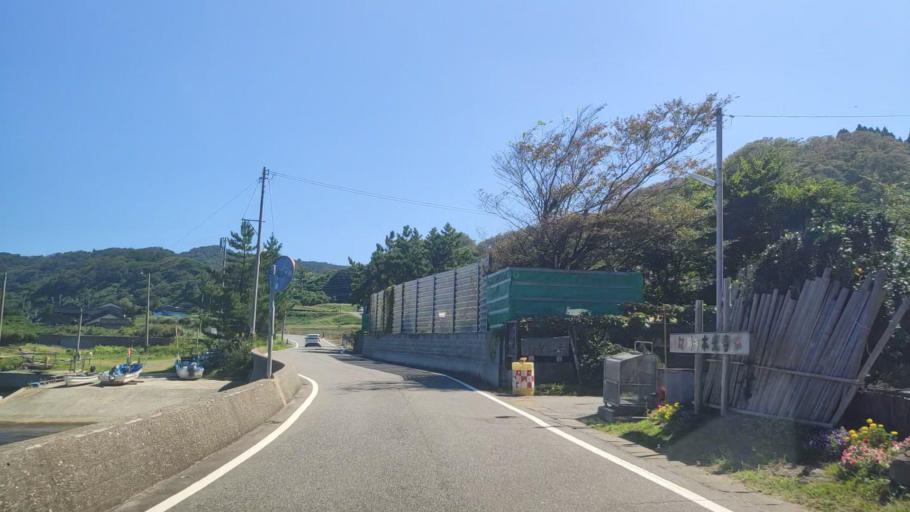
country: JP
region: Ishikawa
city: Nanao
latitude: 37.5064
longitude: 137.2024
